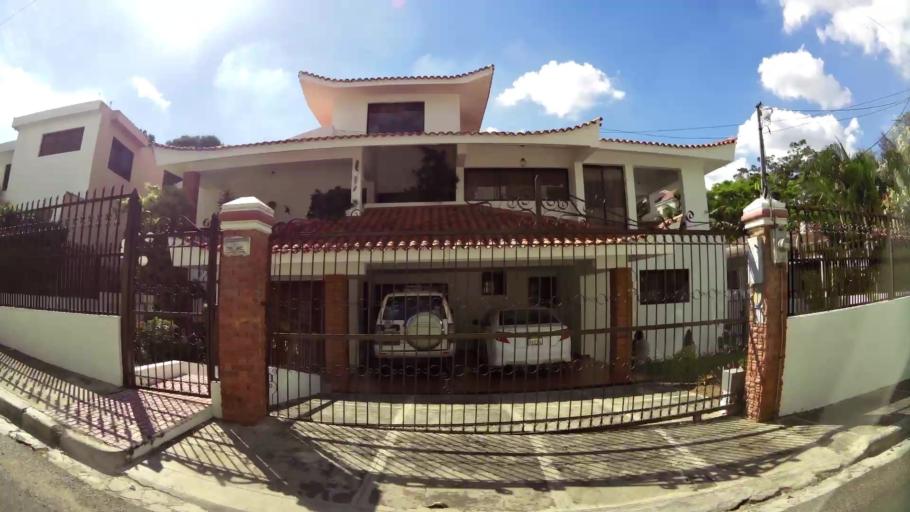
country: DO
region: Santiago
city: Santiago de los Caballeros
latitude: 19.4554
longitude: -70.6810
